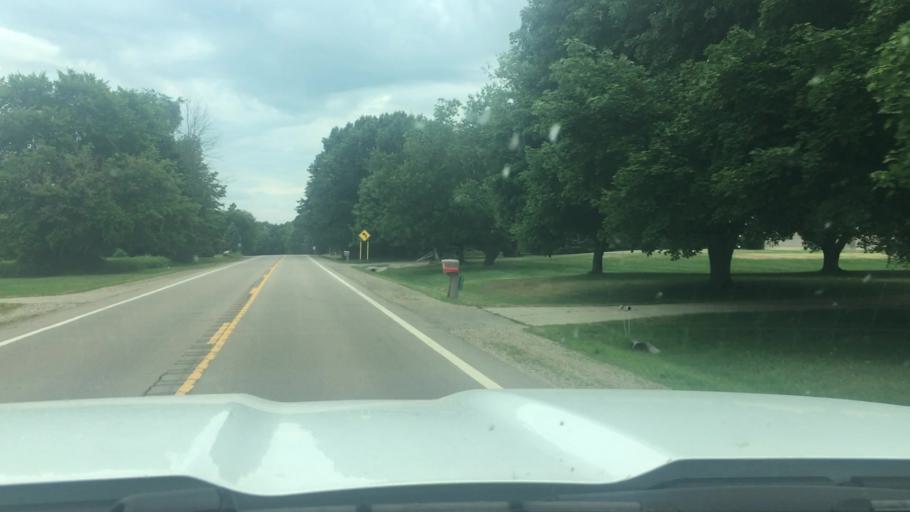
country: US
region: Michigan
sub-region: Ionia County
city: Portland
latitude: 43.0018
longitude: -84.8895
